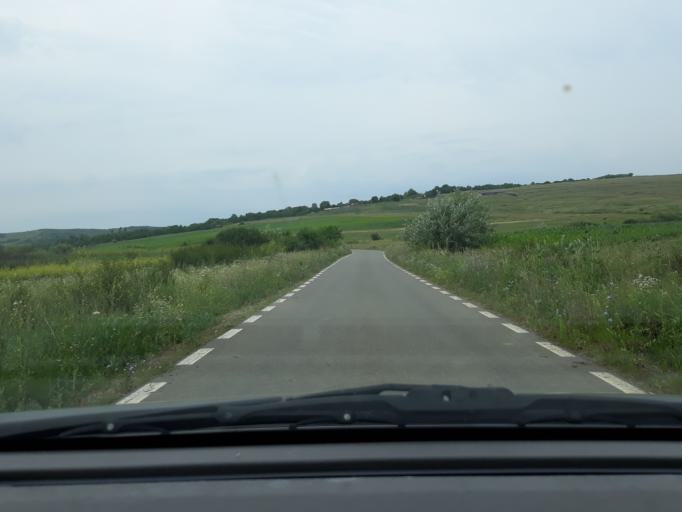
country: RO
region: Salaj
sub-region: Comuna Criseni
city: Criseni
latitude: 47.2690
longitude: 23.0686
